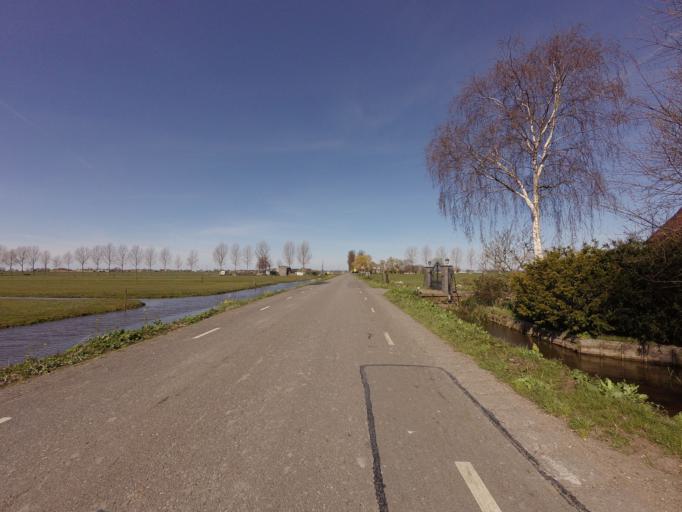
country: NL
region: Utrecht
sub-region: Gemeente De Ronde Venen
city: Mijdrecht
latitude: 52.1919
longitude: 4.8462
